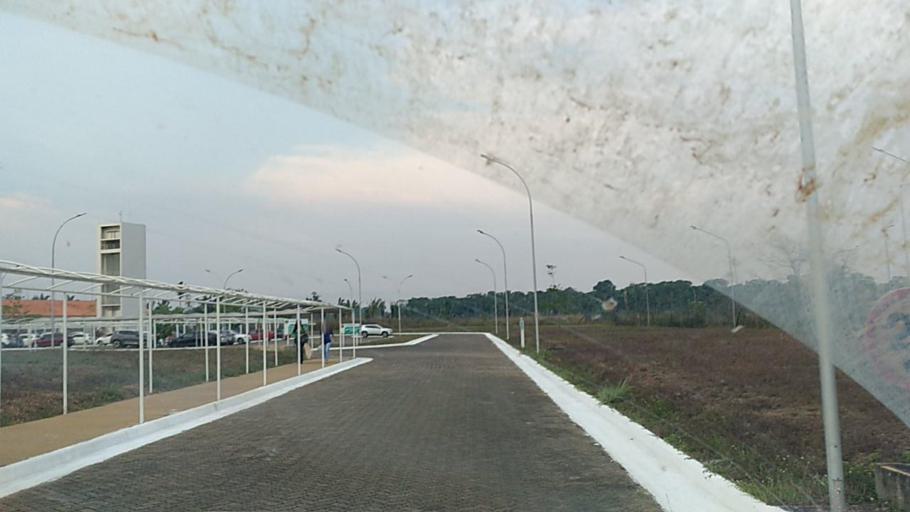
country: BR
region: Rondonia
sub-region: Porto Velho
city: Porto Velho
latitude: -8.7115
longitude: -63.8966
